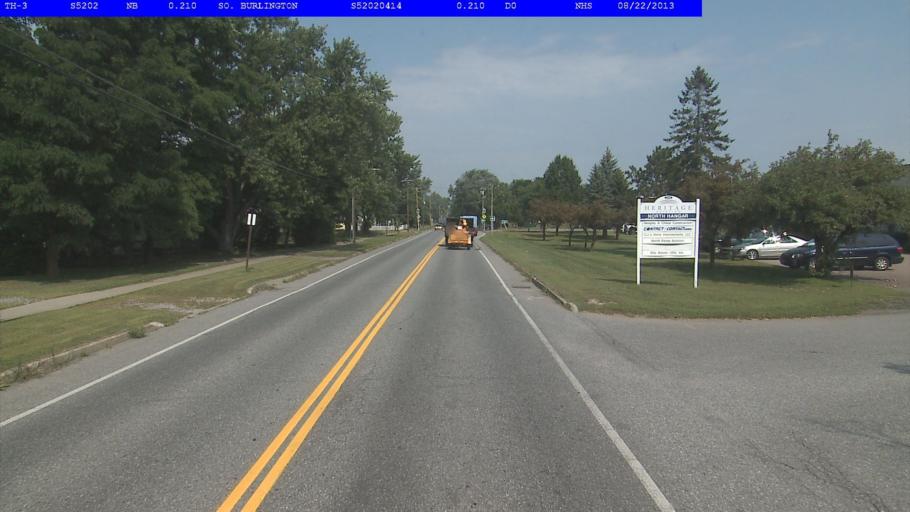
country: US
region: Vermont
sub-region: Chittenden County
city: South Burlington
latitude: 44.4660
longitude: -73.1553
